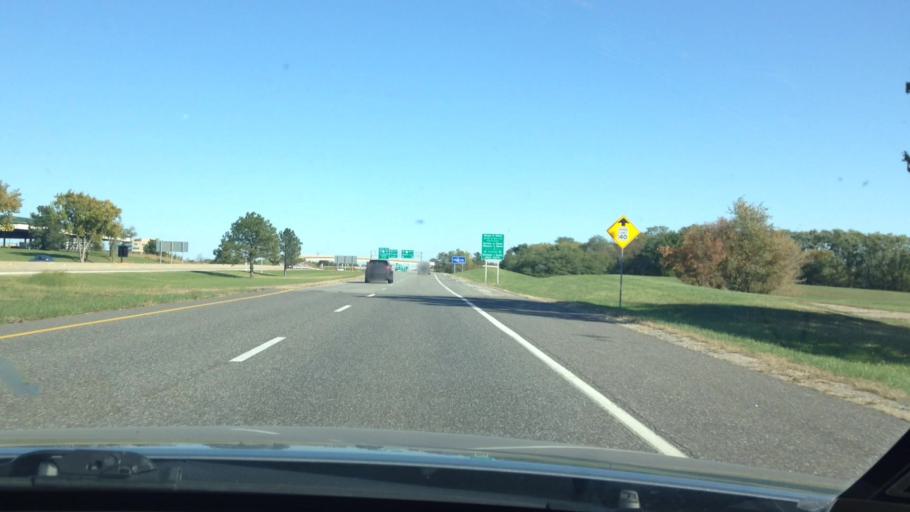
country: US
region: Missouri
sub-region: Platte County
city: Weatherby Lake
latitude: 39.3108
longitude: -94.6963
